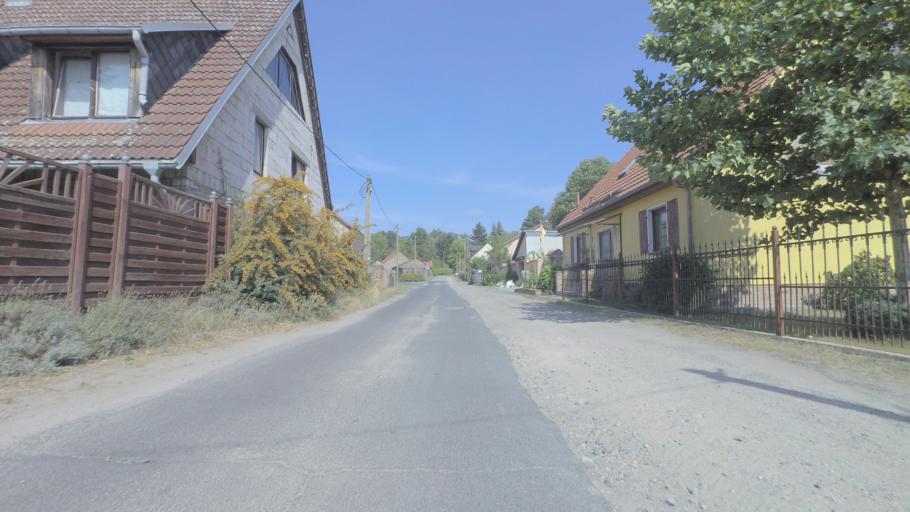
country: DE
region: Brandenburg
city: Sperenberg
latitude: 52.1906
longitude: 13.3293
